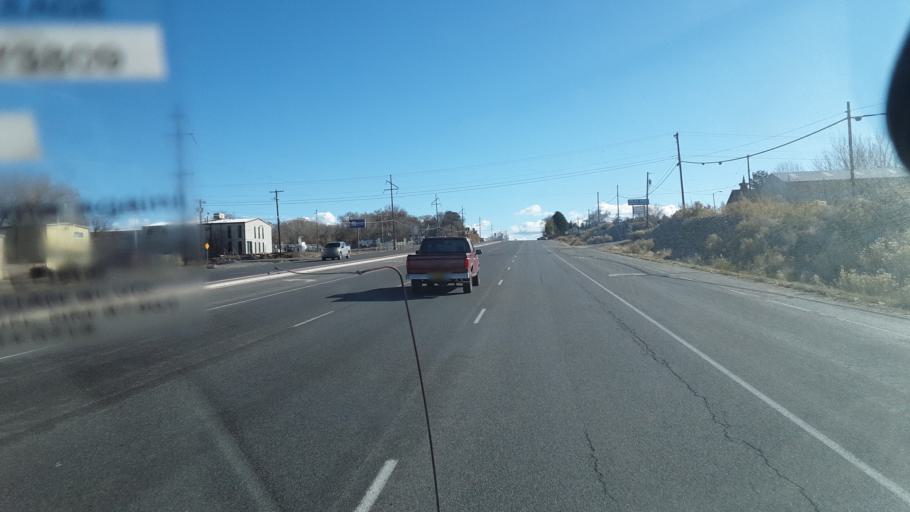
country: US
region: New Mexico
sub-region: San Juan County
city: Lee Acres
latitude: 36.7010
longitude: -108.0614
